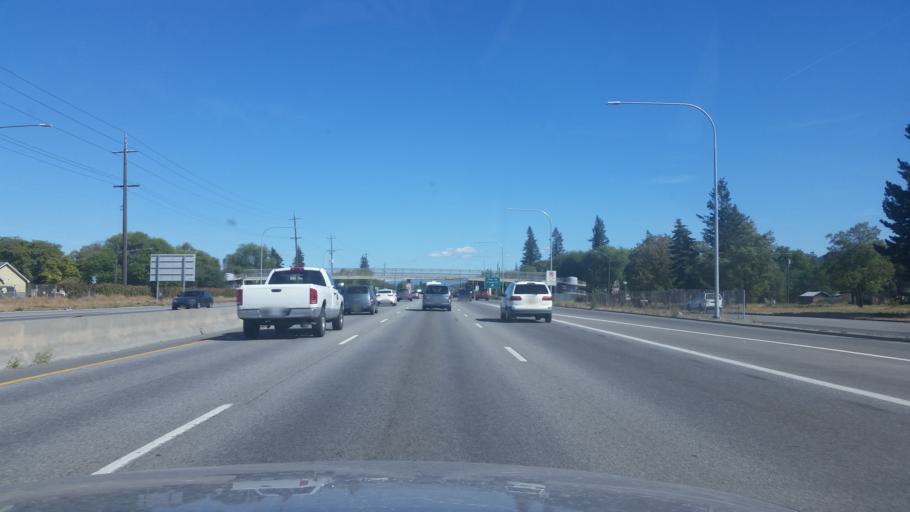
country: US
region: Washington
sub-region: Spokane County
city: Spokane
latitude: 47.6540
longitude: -117.3706
